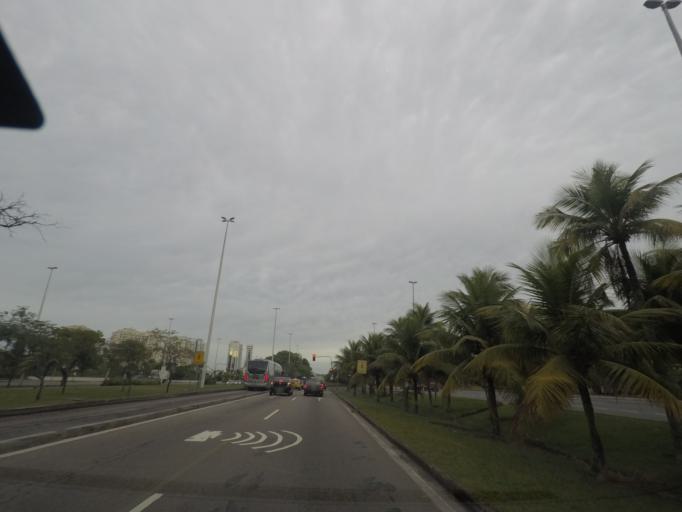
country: BR
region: Rio de Janeiro
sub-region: Nilopolis
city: Nilopolis
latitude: -23.0001
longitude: -43.3960
